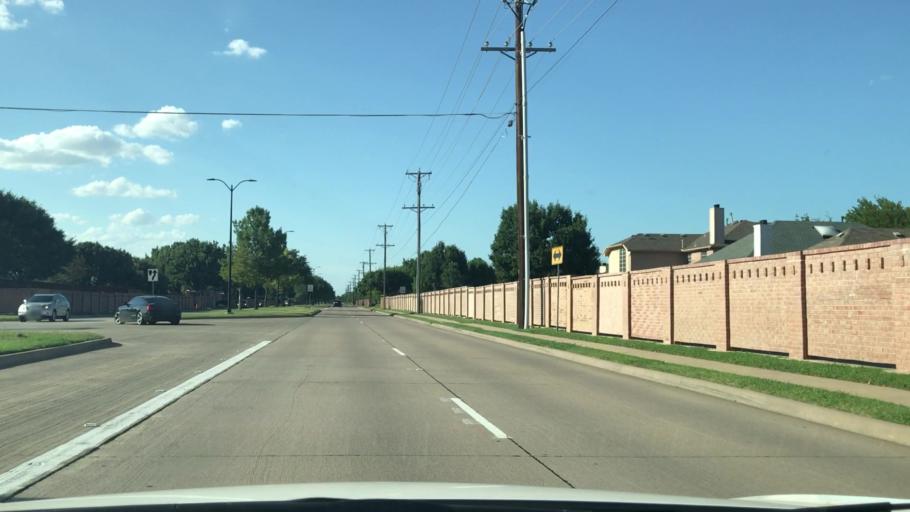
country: US
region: Texas
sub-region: Collin County
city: Frisco
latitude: 33.1087
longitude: -96.7881
